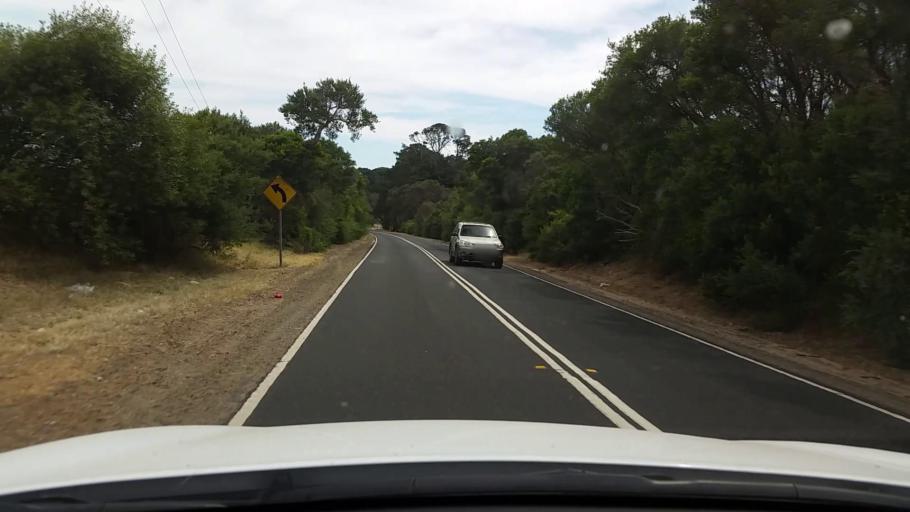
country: AU
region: Victoria
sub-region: Mornington Peninsula
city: Rosebud West
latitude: -38.4373
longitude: 144.8969
